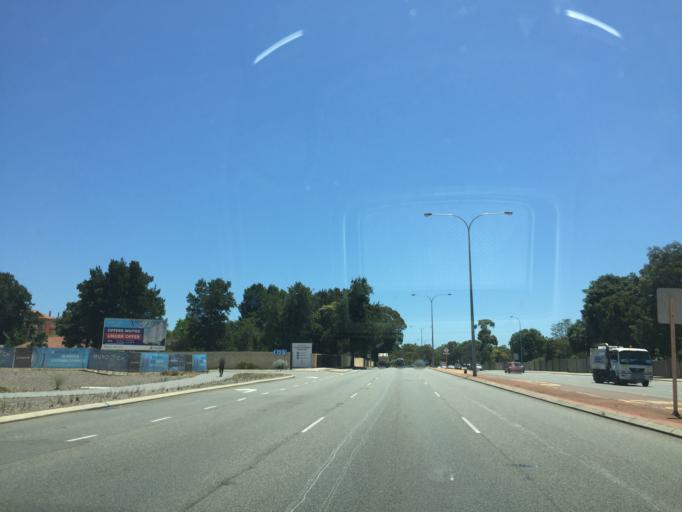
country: AU
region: Western Australia
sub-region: Melville
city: Winthrop
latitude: -32.0659
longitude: 115.8479
